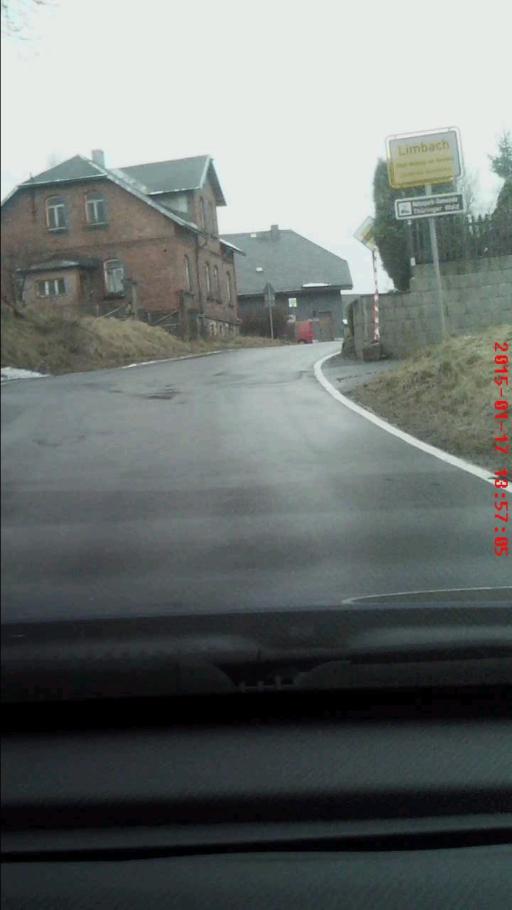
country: DE
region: Thuringia
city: Steinheid
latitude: 50.4768
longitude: 11.0691
